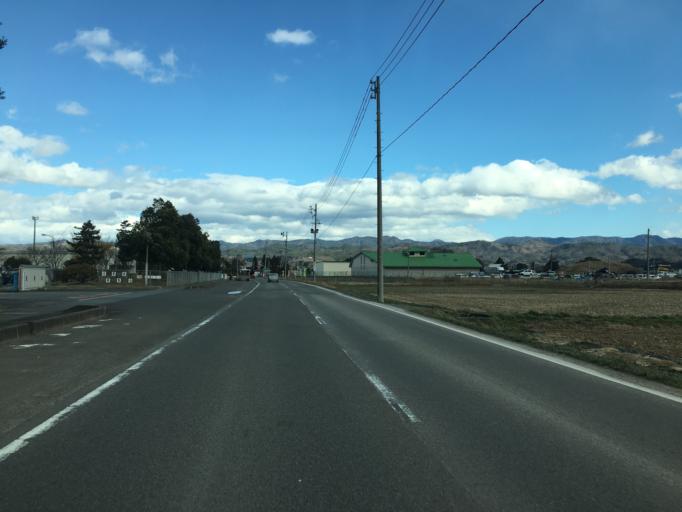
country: JP
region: Fukushima
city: Yanagawamachi-saiwaicho
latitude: 37.8569
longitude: 140.5864
